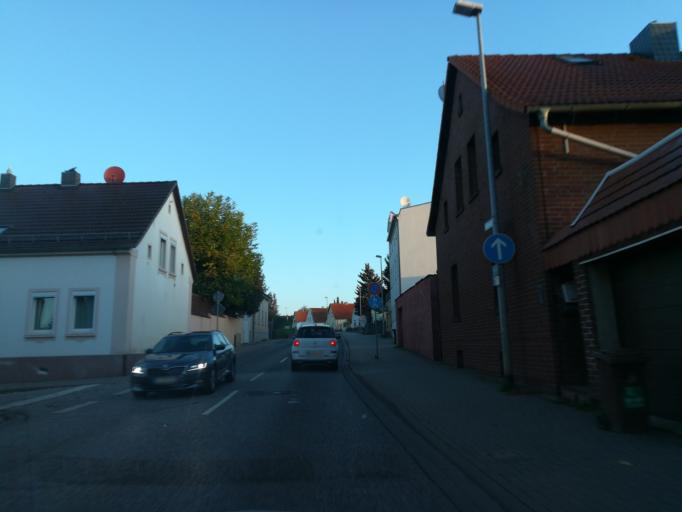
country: DE
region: Saxony-Anhalt
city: Diesdorf
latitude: 52.1318
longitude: 11.5736
